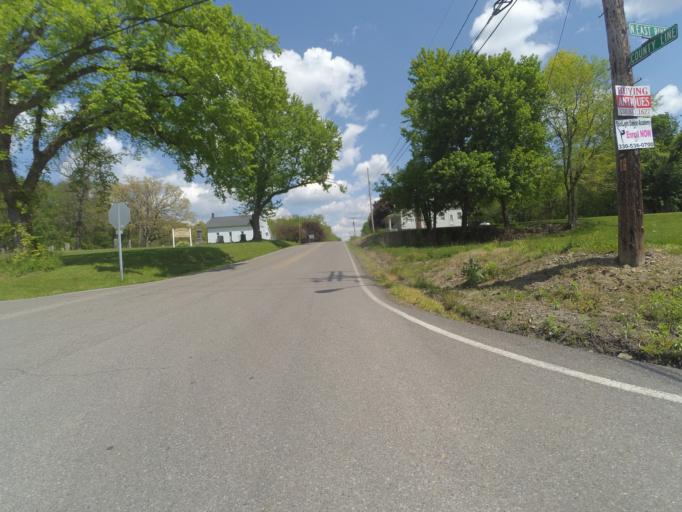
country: US
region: Ohio
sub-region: Mahoning County
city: Craig Beach
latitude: 41.1342
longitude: -80.9662
